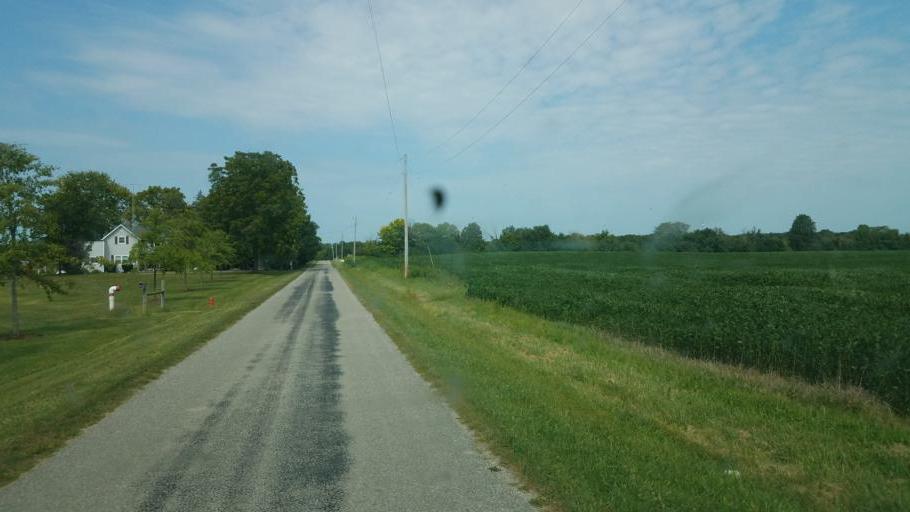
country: US
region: Ohio
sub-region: Delaware County
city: Ashley
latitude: 40.4451
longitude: -83.0329
